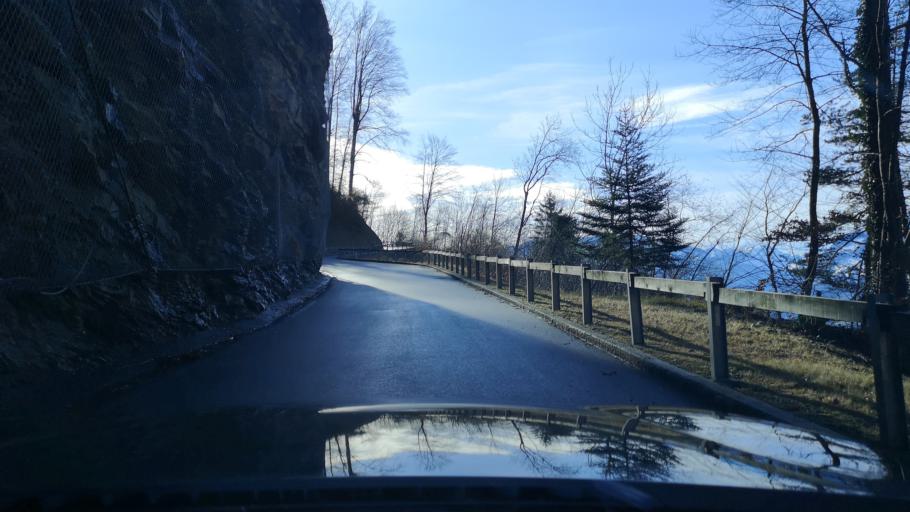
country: LI
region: Triesenberg
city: Triesenberg
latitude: 47.1236
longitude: 9.5364
